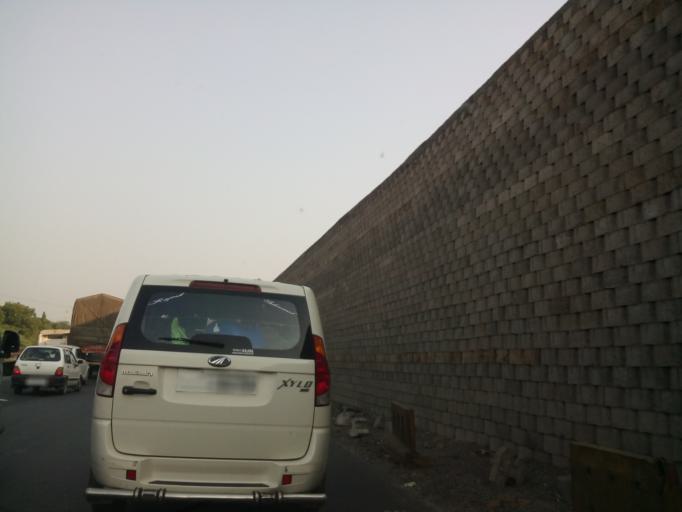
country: IN
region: Gujarat
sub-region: Vadodara
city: Vadodara
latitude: 22.3635
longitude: 73.1943
